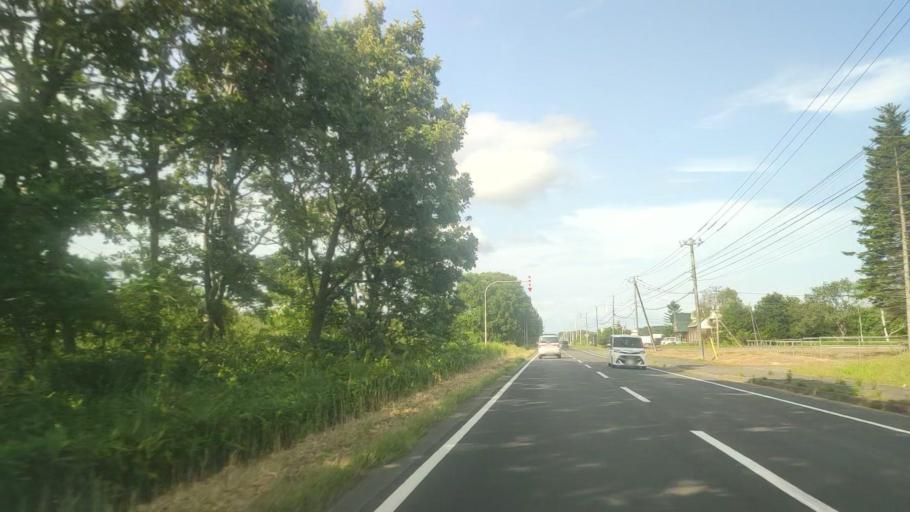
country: JP
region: Hokkaido
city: Chitose
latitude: 42.7405
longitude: 141.7836
